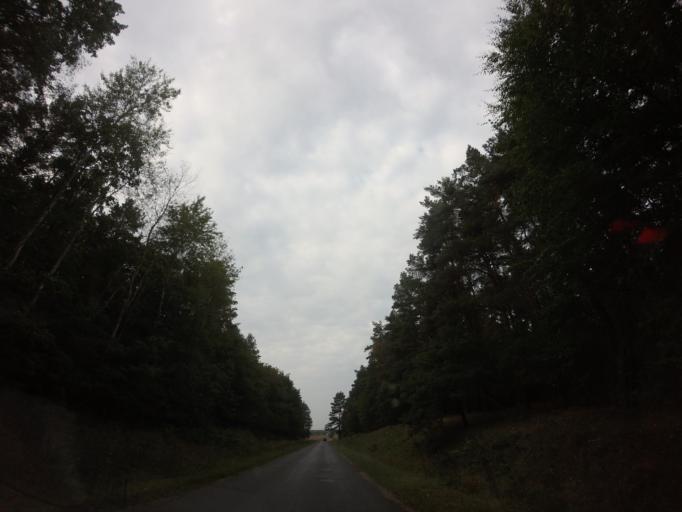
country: PL
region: West Pomeranian Voivodeship
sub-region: Powiat drawski
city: Drawsko Pomorskie
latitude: 53.4862
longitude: 15.7771
